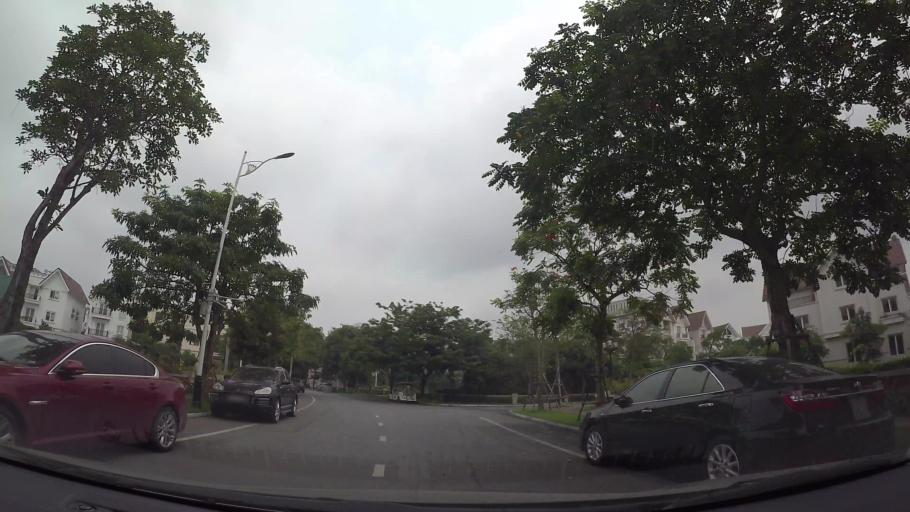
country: VN
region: Ha Noi
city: Trau Quy
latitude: 21.0412
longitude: 105.9212
